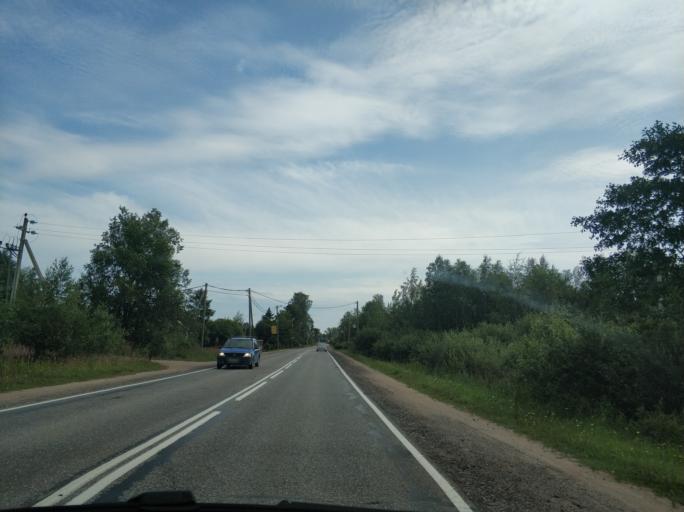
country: RU
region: Leningrad
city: Borisova Griva
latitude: 60.0921
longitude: 30.9597
